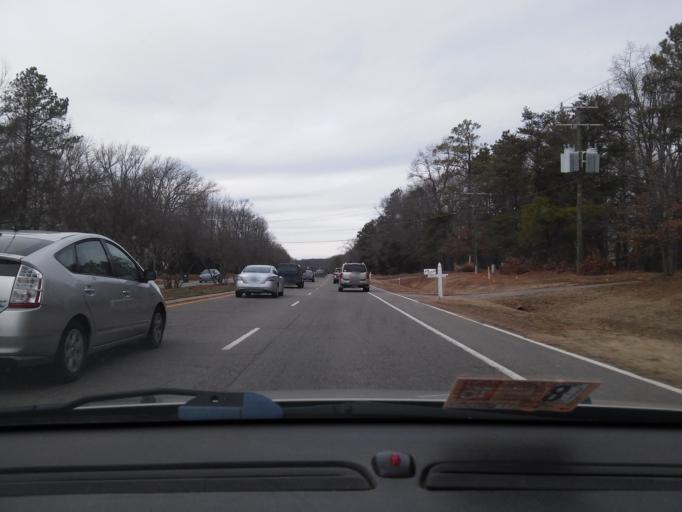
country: US
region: Virginia
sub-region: Chesterfield County
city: Bon Air
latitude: 37.5308
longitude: -77.6298
